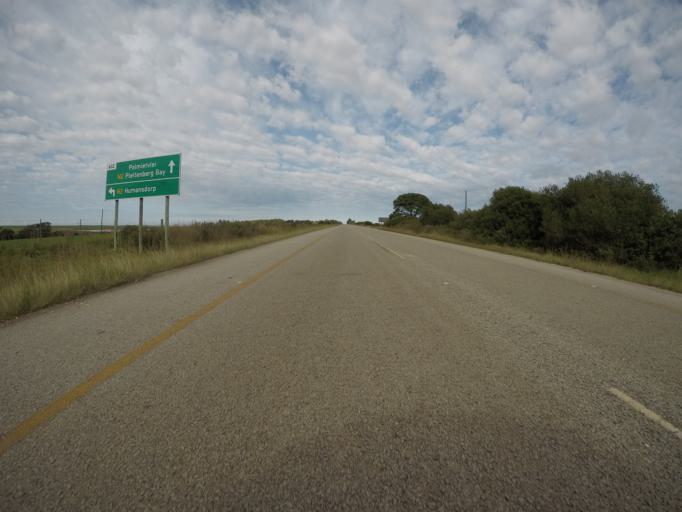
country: ZA
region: Eastern Cape
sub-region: Cacadu District Municipality
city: Kareedouw
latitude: -34.0481
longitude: 24.4572
